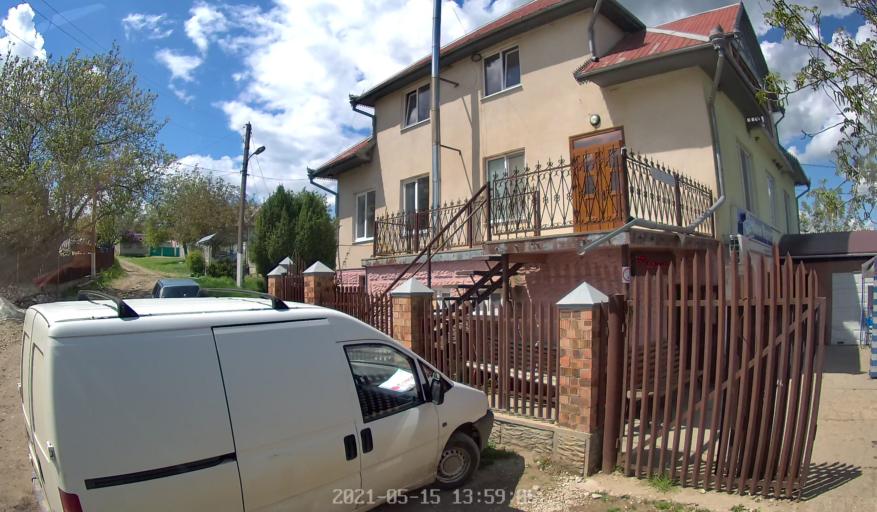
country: MD
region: Hincesti
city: Hincesti
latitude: 46.7423
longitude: 28.5129
